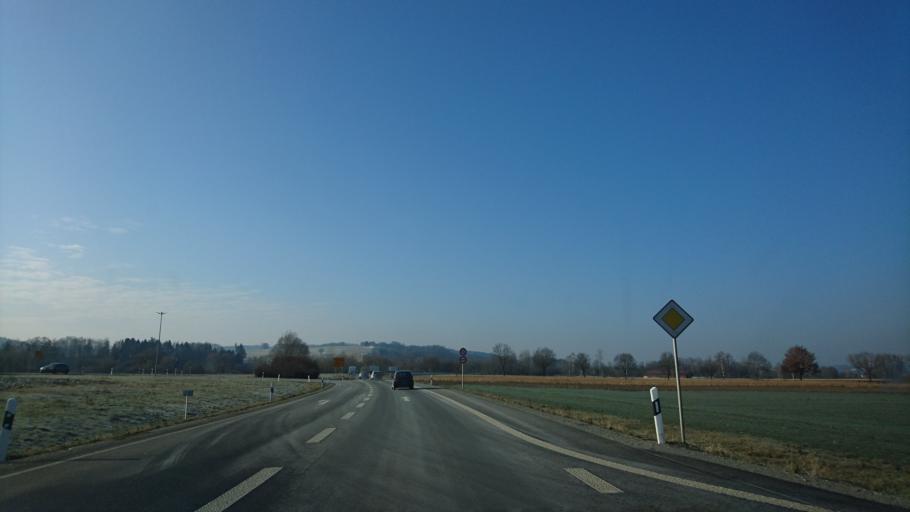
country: DE
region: Bavaria
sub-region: Lower Bavaria
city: Bad Birnbach
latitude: 48.4328
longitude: 13.0952
